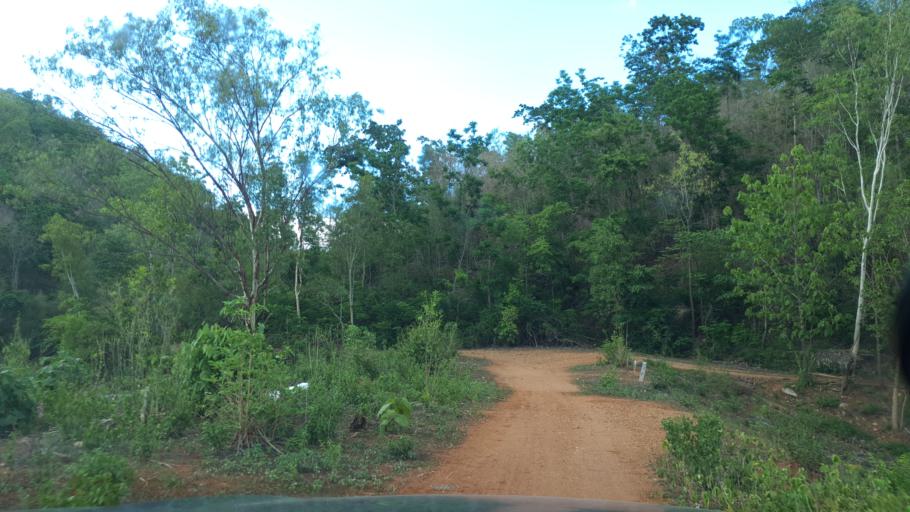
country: TH
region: Lampang
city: Sop Prap
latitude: 17.8893
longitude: 99.2845
